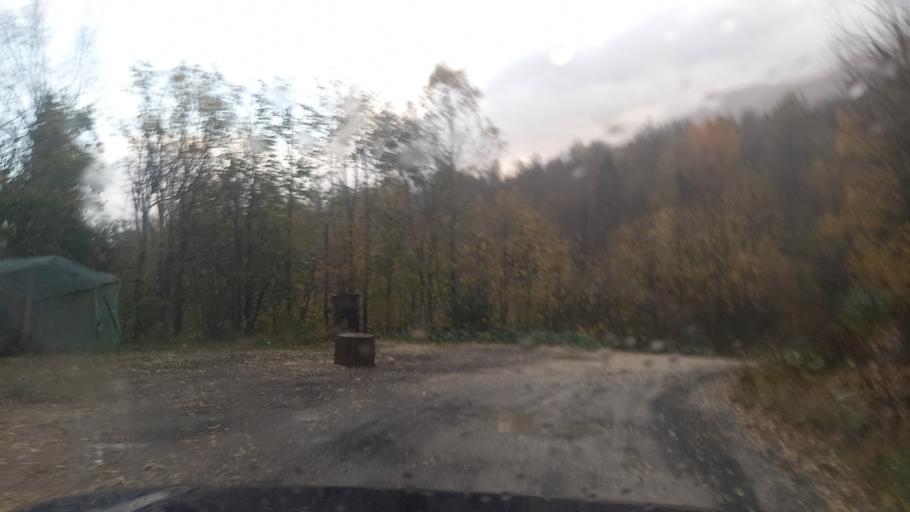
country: RU
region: Krasnodarskiy
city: Neftegorsk
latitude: 44.0177
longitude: 39.8442
